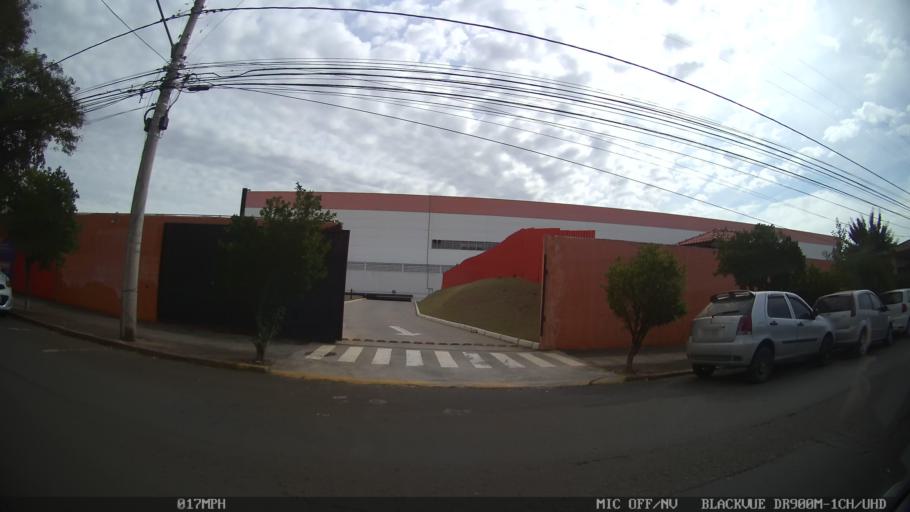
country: BR
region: Sao Paulo
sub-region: Piracicaba
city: Piracicaba
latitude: -22.7114
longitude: -47.6546
